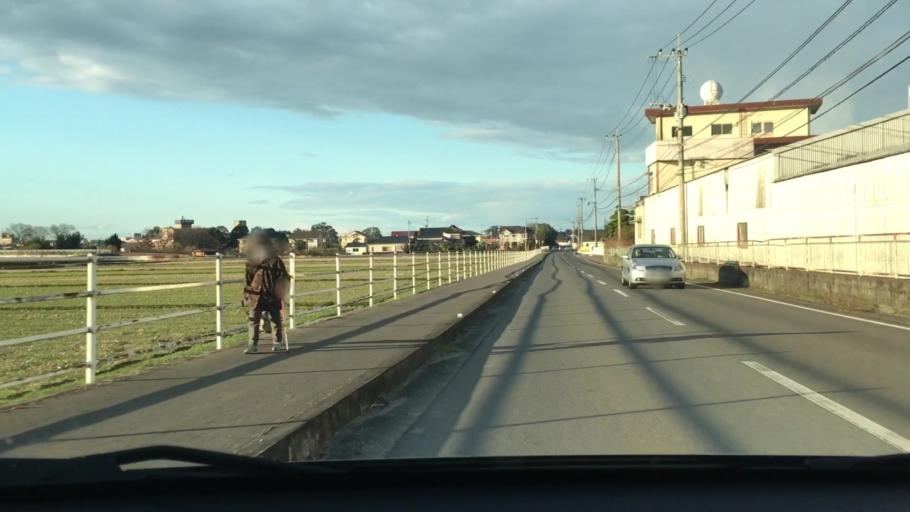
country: JP
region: Oita
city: Bungo-Takada-shi
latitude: 33.5187
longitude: 131.3483
